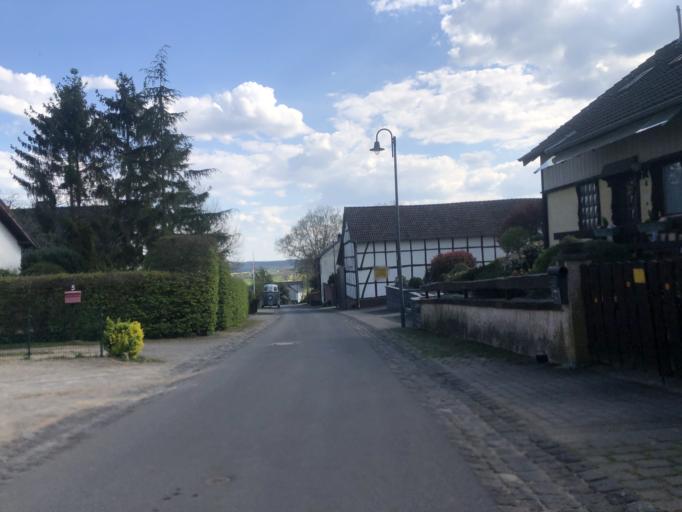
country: DE
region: North Rhine-Westphalia
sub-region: Regierungsbezirk Koln
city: Kall
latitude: 50.6070
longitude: 6.5469
